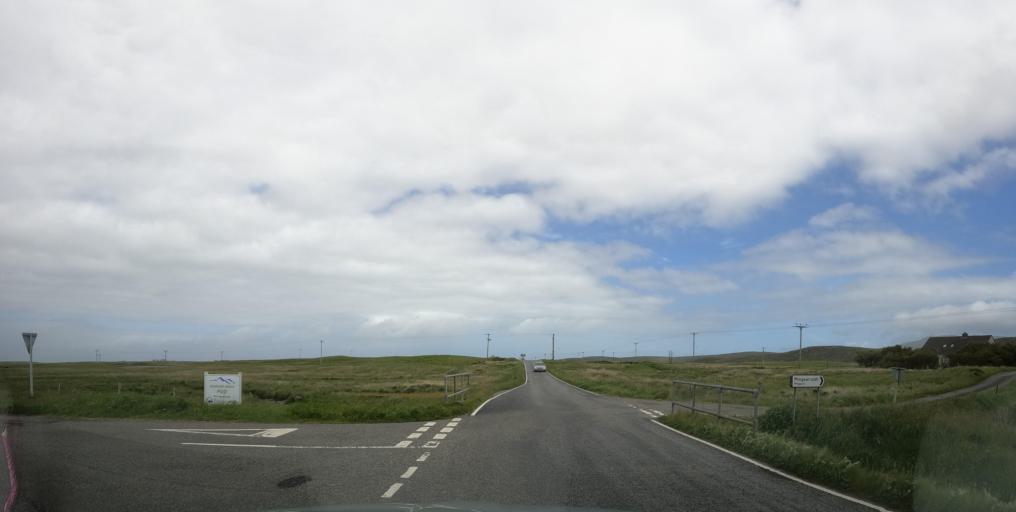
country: GB
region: Scotland
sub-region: Eilean Siar
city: Isle of South Uist
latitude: 57.2113
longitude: -7.3941
